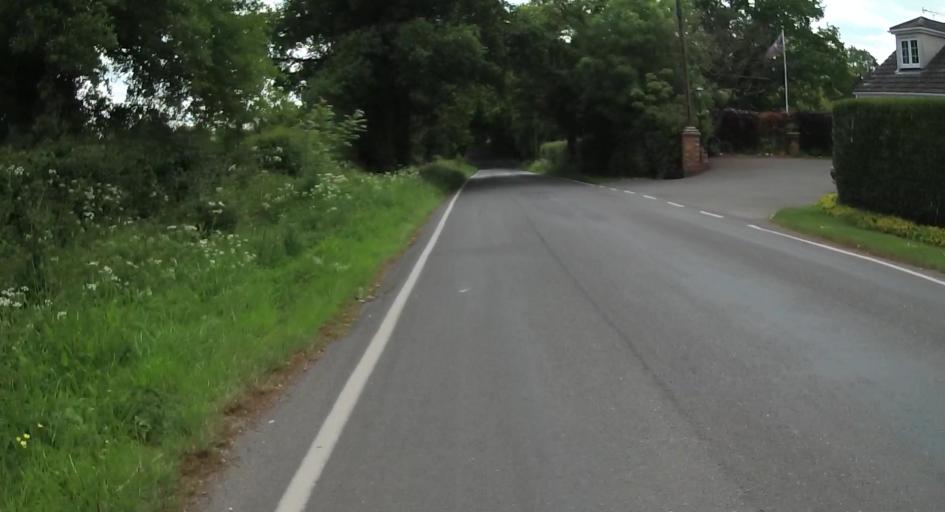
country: GB
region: England
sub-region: Surrey
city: Farnham
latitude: 51.2280
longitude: -0.8365
